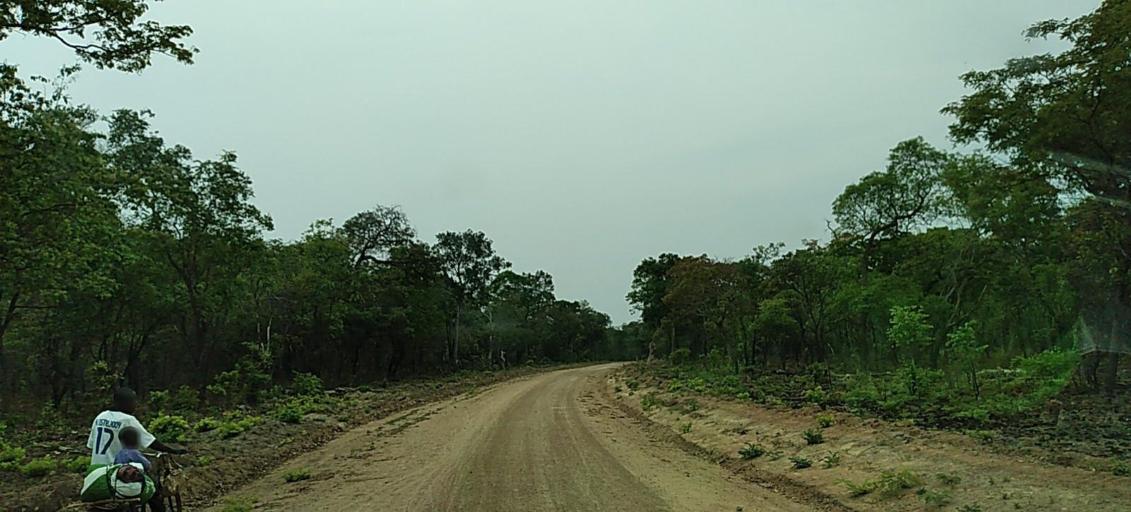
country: ZM
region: North-Western
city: Solwezi
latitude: -12.5227
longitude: 26.5237
